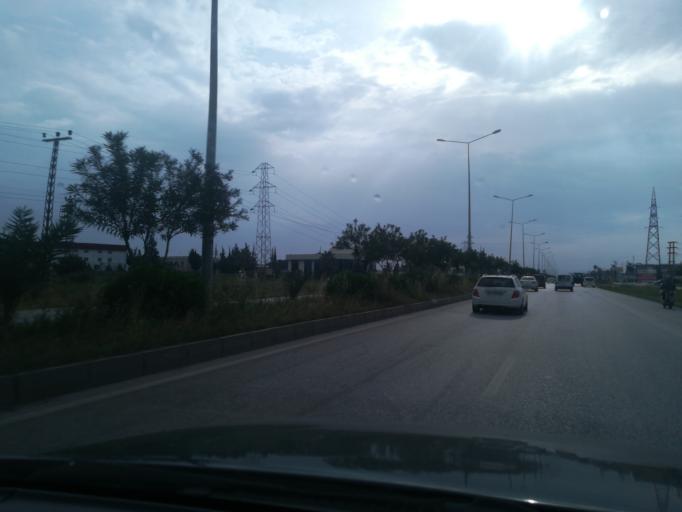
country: TR
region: Adana
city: Yuregir
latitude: 36.9828
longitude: 35.4077
